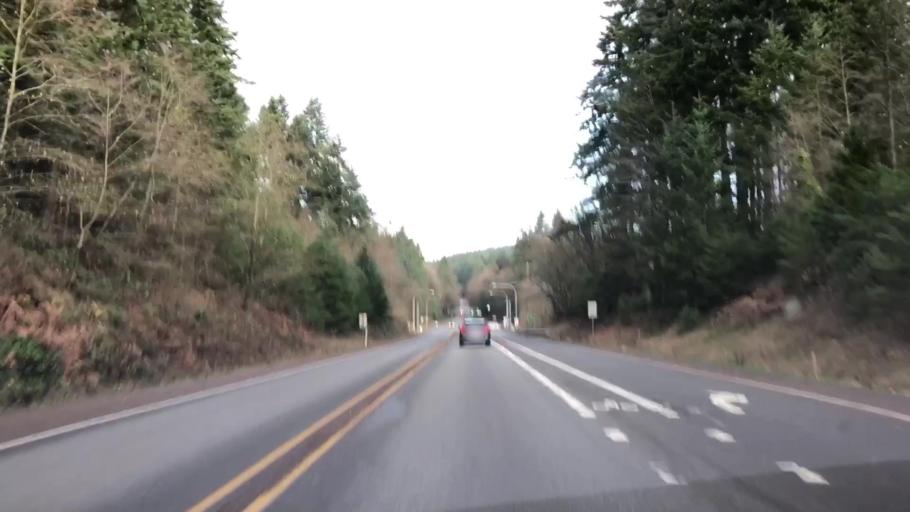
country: US
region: Washington
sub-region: Kitsap County
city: Bainbridge Island
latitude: 47.6514
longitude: -122.5232
